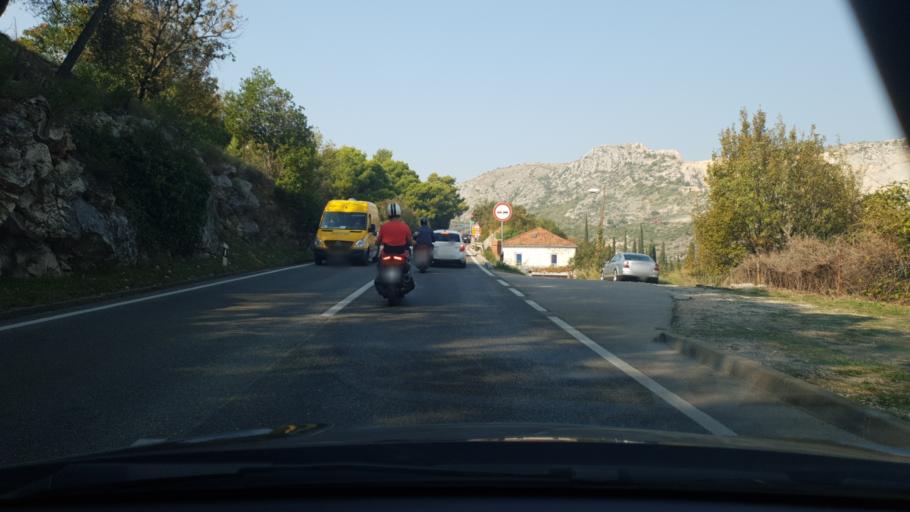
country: HR
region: Dubrovacko-Neretvanska
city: Cibaca
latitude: 42.6280
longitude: 18.1652
